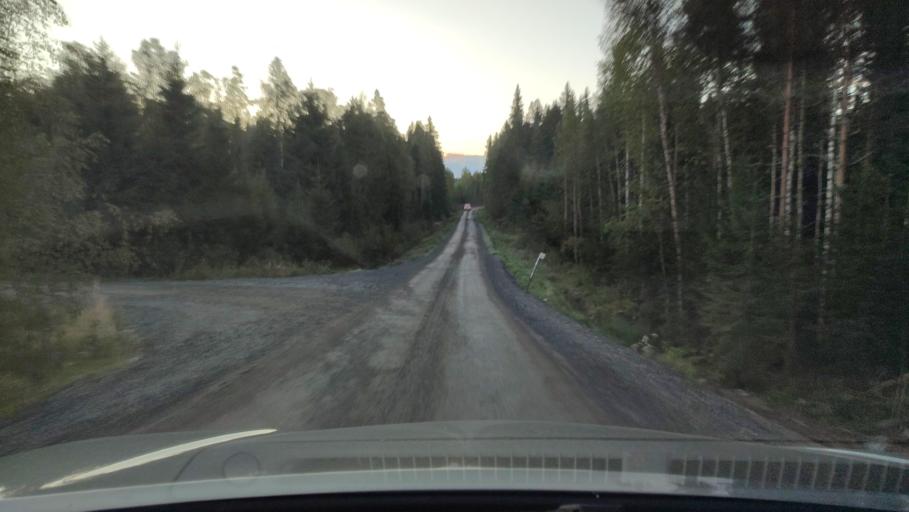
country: FI
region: Southern Ostrobothnia
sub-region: Suupohja
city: Karijoki
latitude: 62.2003
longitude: 21.5680
